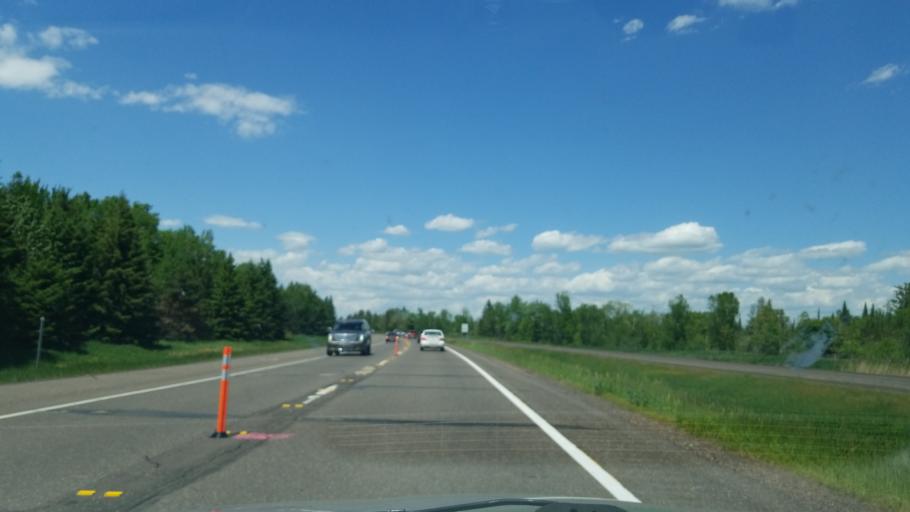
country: US
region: Minnesota
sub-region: Pine County
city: Sandstone
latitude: 46.2880
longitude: -92.8201
